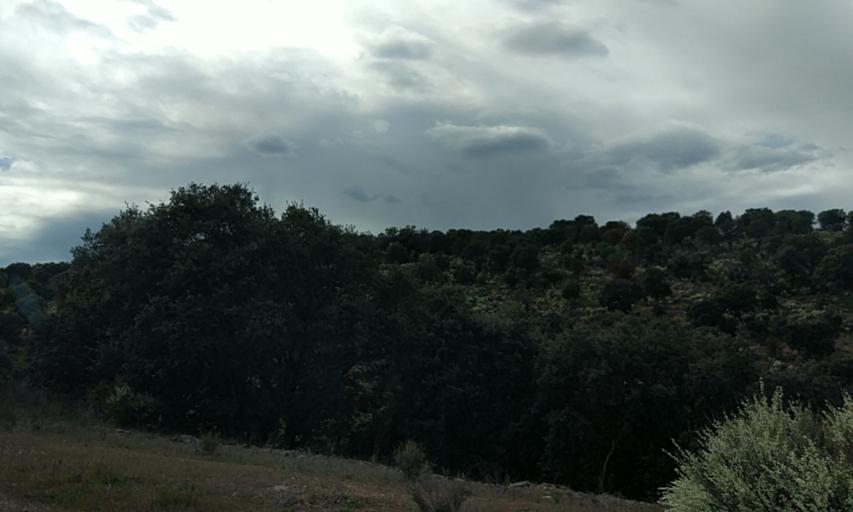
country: ES
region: Castille and Leon
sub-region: Provincia de Salamanca
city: Pastores
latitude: 40.5052
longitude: -6.5753
